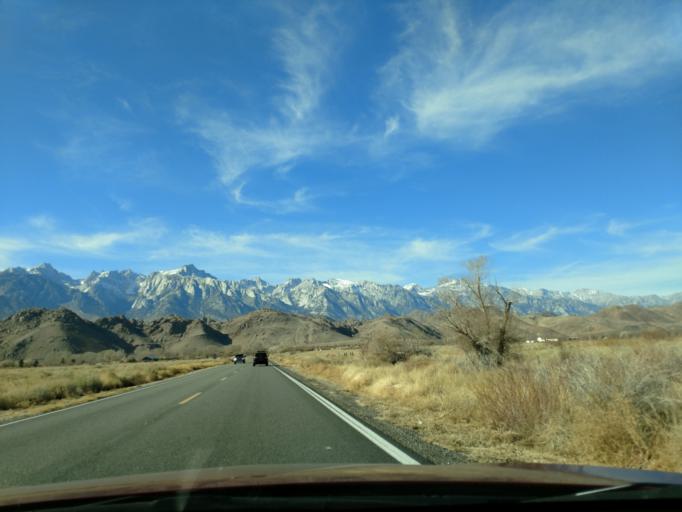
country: US
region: California
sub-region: Inyo County
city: Lone Pine
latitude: 36.5793
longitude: -118.0475
